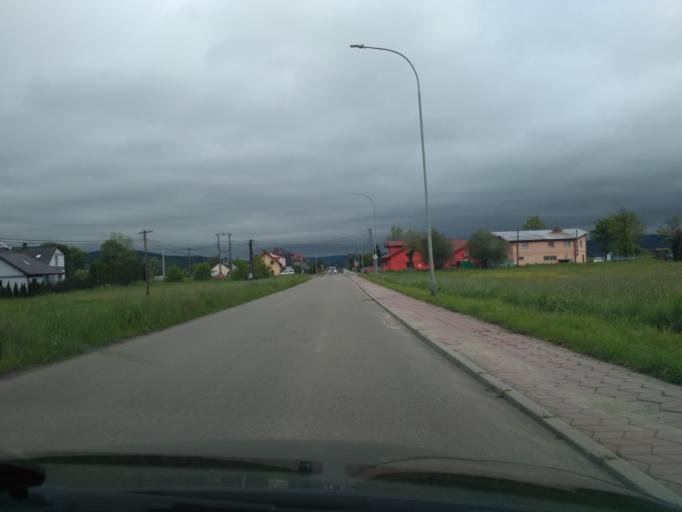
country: PL
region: Subcarpathian Voivodeship
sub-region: Powiat jasielski
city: Brzyska
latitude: 49.8199
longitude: 21.3930
